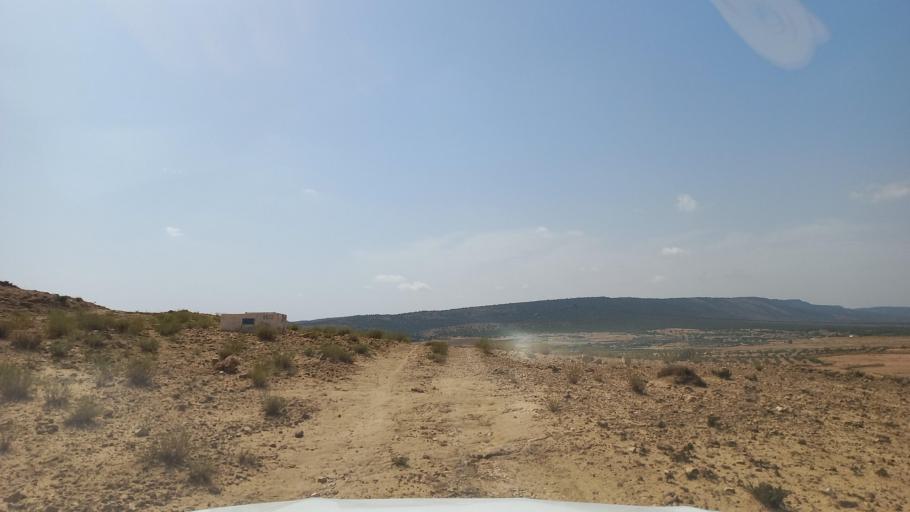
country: TN
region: Al Qasrayn
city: Sbiba
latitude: 35.3989
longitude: 8.9740
